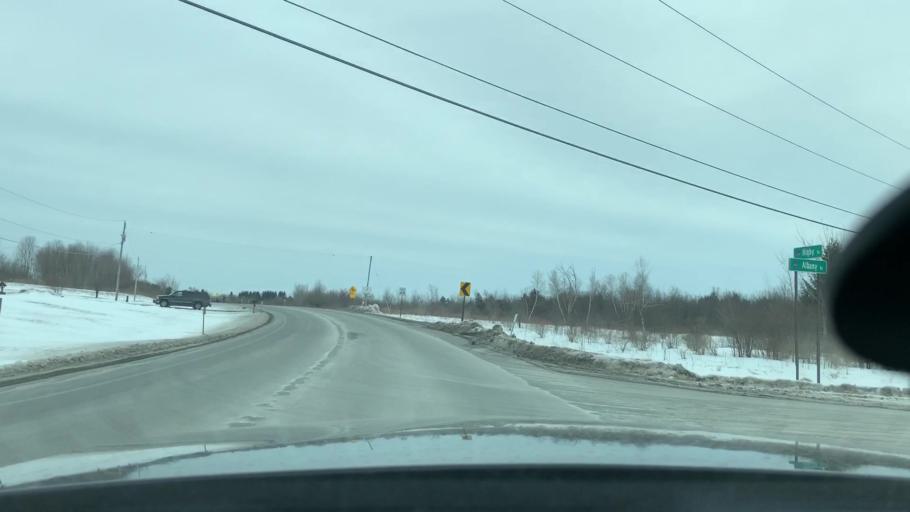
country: US
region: New York
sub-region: Oneida County
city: Utica
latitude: 43.0335
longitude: -75.1842
